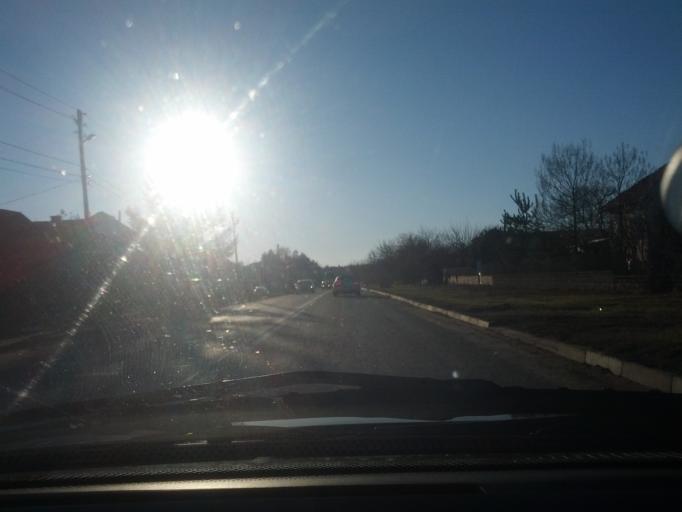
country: BG
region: Vratsa
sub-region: Obshtina Borovan
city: Borovan
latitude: 43.4198
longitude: 23.7445
